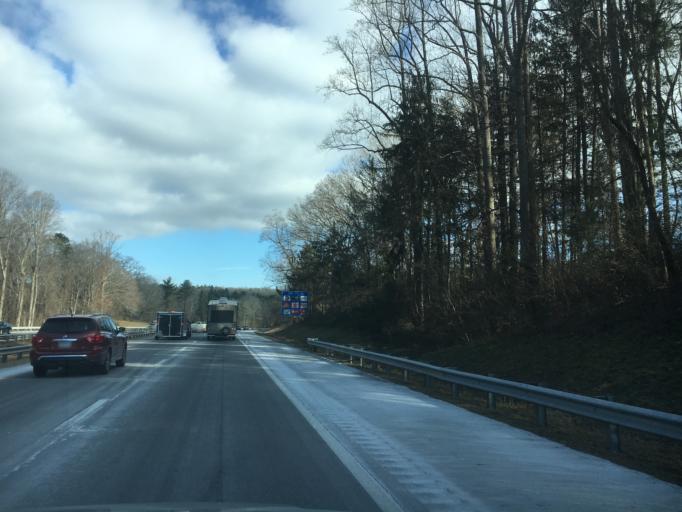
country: US
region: North Carolina
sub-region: Buncombe County
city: Biltmore Forest
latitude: 35.5579
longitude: -82.5593
